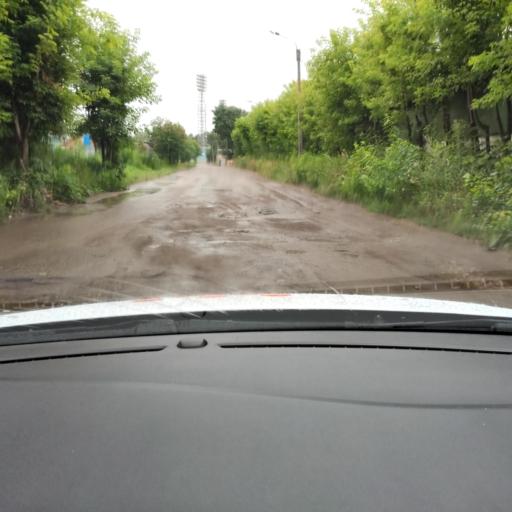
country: RU
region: Tatarstan
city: Vysokaya Gora
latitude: 55.8754
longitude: 49.2342
